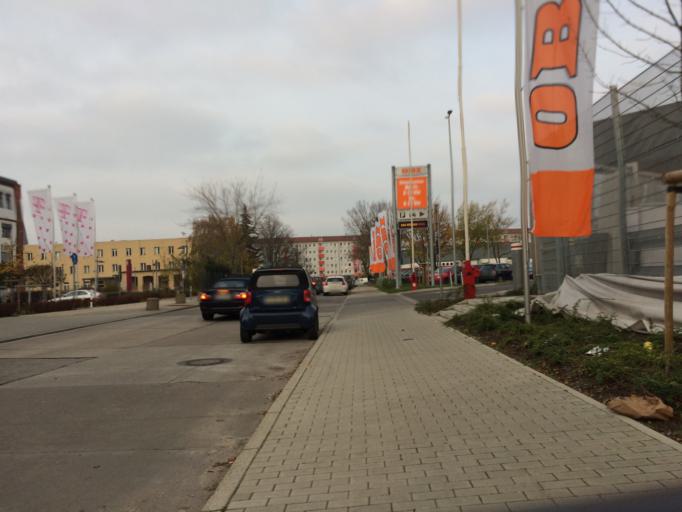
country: DE
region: Berlin
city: Rummelsburg
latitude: 52.5101
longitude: 13.4909
